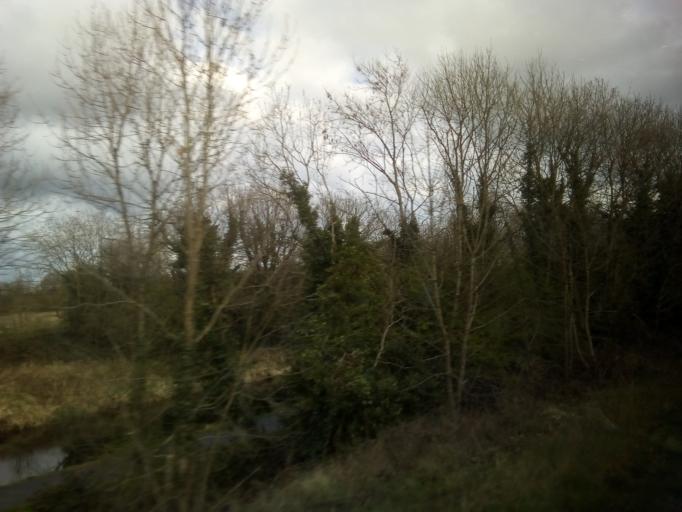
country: IE
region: Leinster
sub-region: An Iarmhi
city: An Muileann gCearr
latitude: 53.5138
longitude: -7.3221
